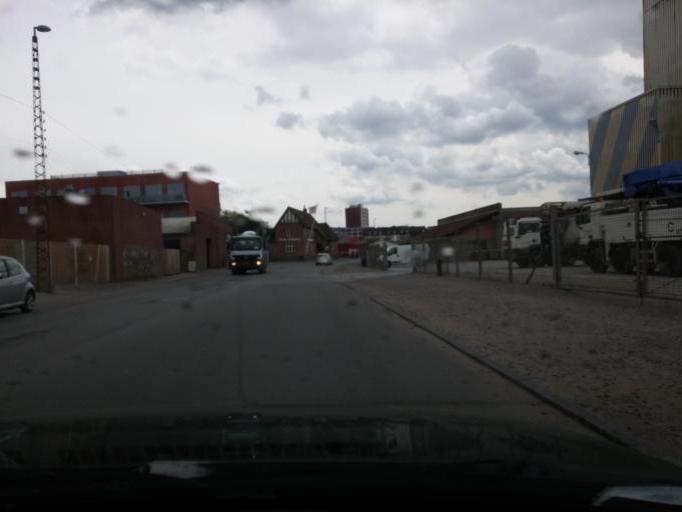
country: DK
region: South Denmark
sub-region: Odense Kommune
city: Odense
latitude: 55.4099
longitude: 10.3847
